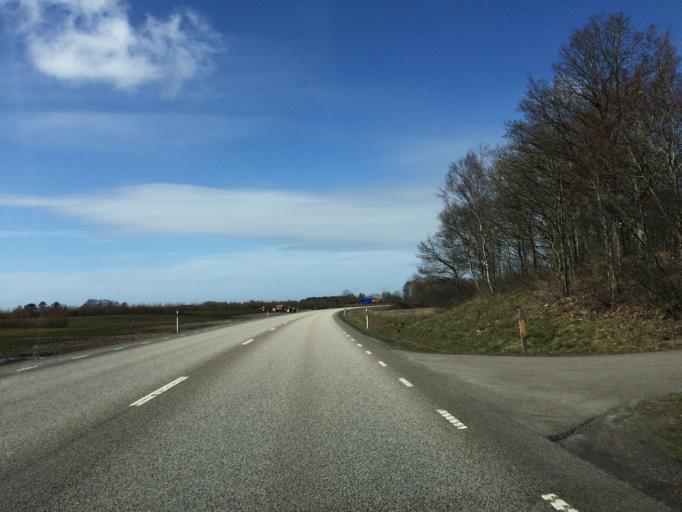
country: SE
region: Halland
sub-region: Laholms Kommun
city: Veinge
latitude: 56.5271
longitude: 13.1776
